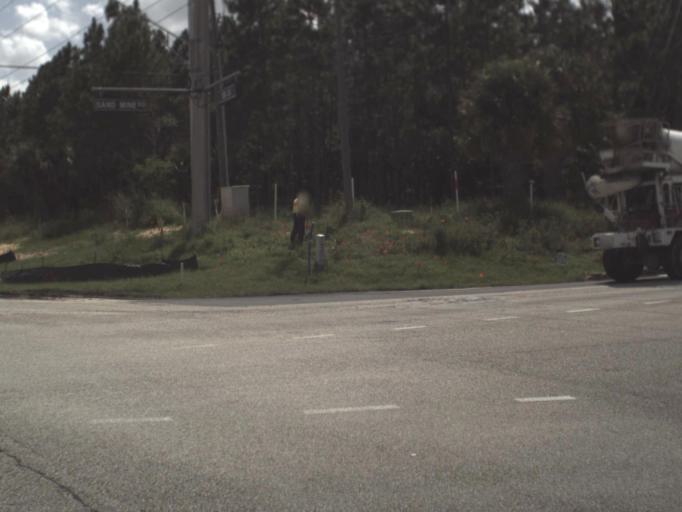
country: US
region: Florida
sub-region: Lake County
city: Four Corners
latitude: 28.3104
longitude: -81.6677
